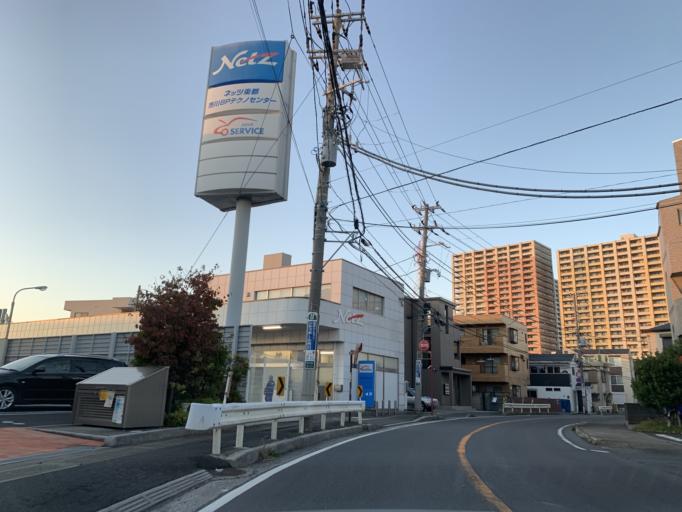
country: JP
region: Chiba
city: Matsudo
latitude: 35.7277
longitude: 139.9002
